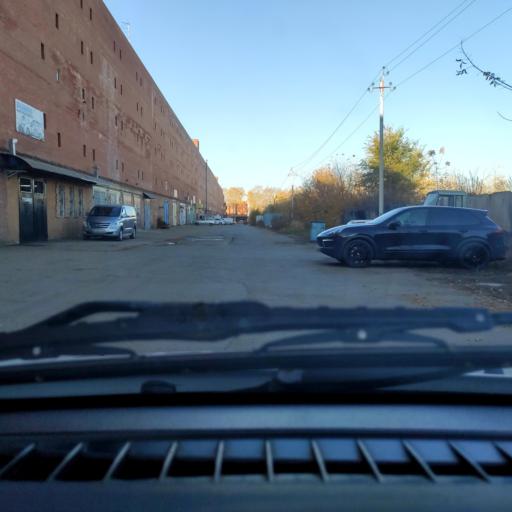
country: RU
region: Samara
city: Tol'yatti
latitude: 53.5397
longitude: 49.3055
